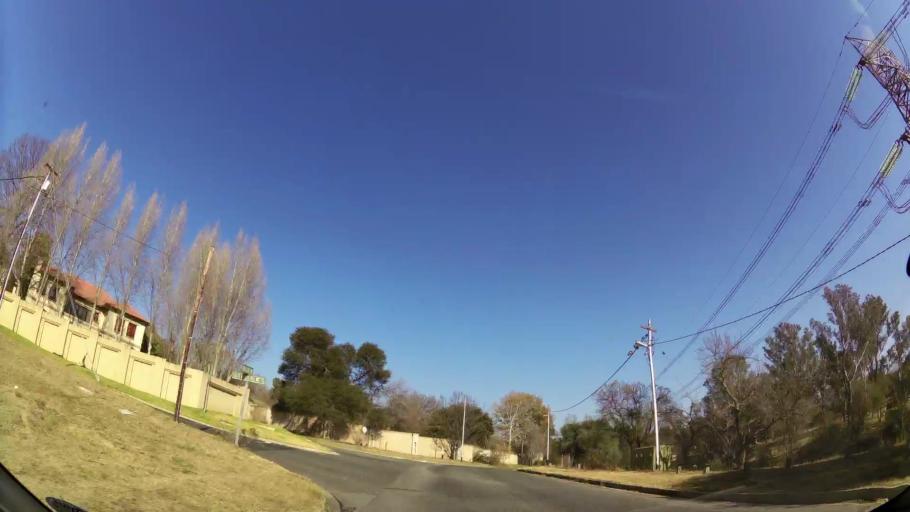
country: ZA
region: Gauteng
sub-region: City of Johannesburg Metropolitan Municipality
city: Midrand
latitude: -26.0615
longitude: 28.0473
